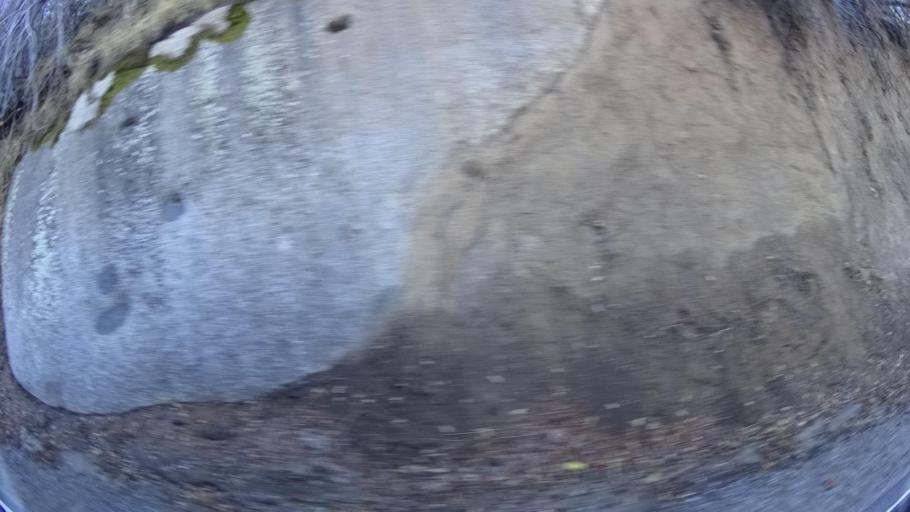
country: US
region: California
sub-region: Kern County
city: Alta Sierra
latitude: 35.7375
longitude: -118.6486
